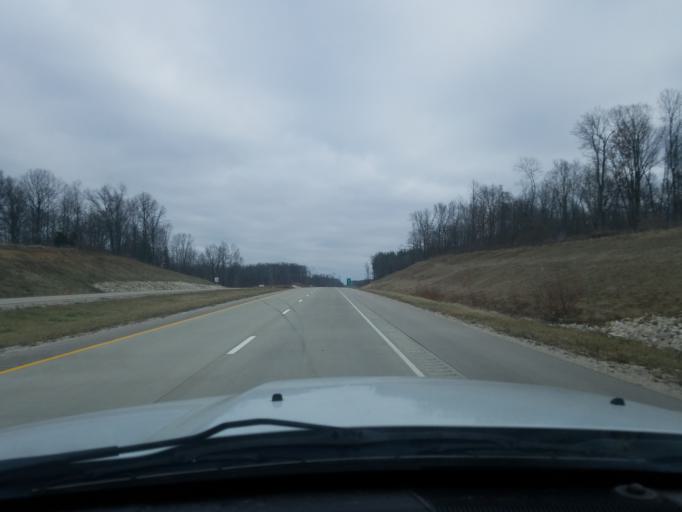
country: US
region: Indiana
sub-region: Greene County
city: Bloomfield
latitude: 38.9695
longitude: -86.7583
